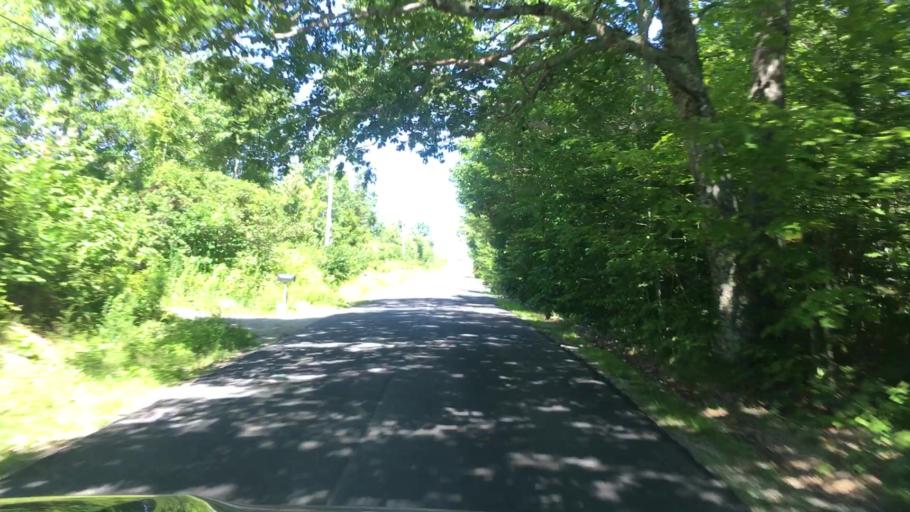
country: US
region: Maine
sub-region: Hancock County
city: Sedgwick
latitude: 44.3210
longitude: -68.6311
